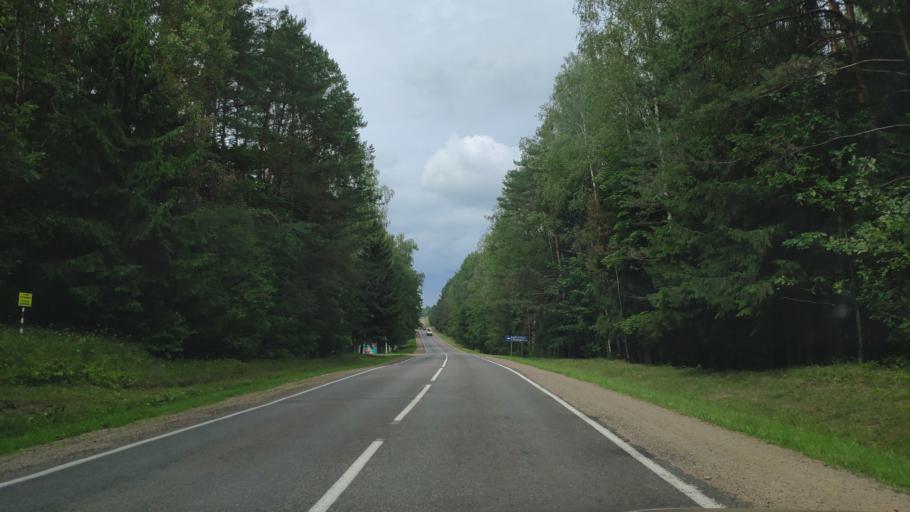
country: BY
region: Minsk
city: Novosel'ye
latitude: 53.9514
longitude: 27.2459
